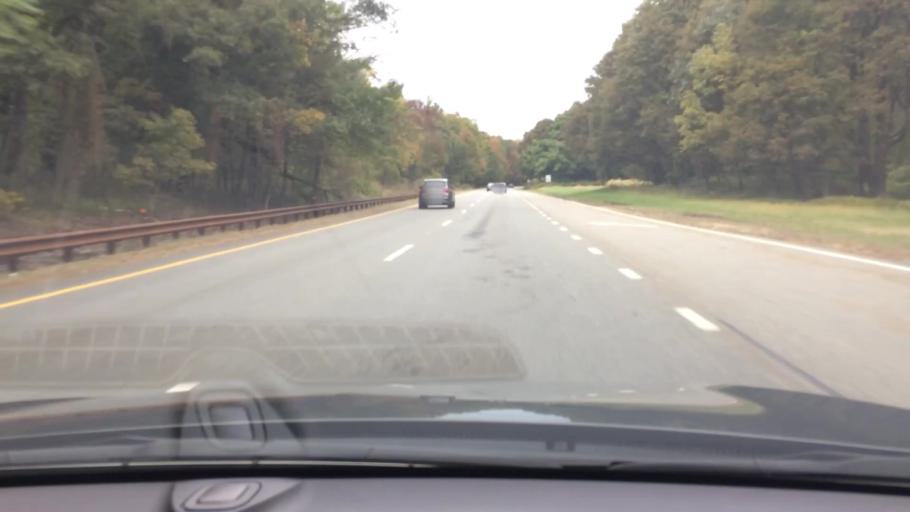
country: US
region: New Jersey
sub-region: Bergen County
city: Alpine
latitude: 40.9603
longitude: -73.9183
